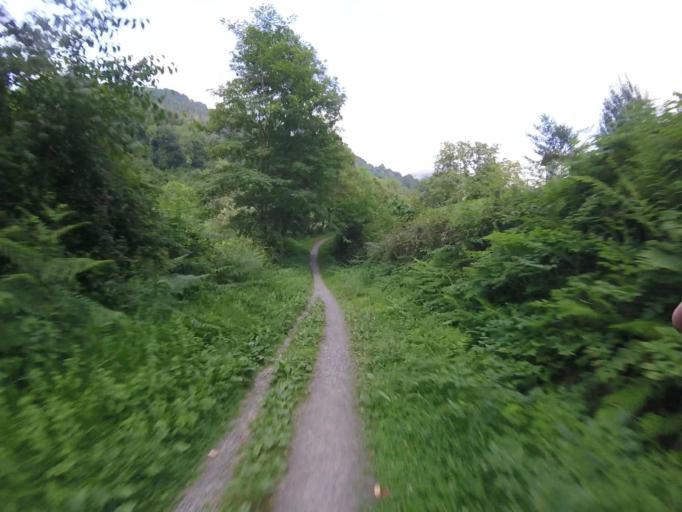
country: ES
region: Basque Country
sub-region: Provincia de Guipuzcoa
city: Astigarraga
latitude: 43.2439
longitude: -1.9424
